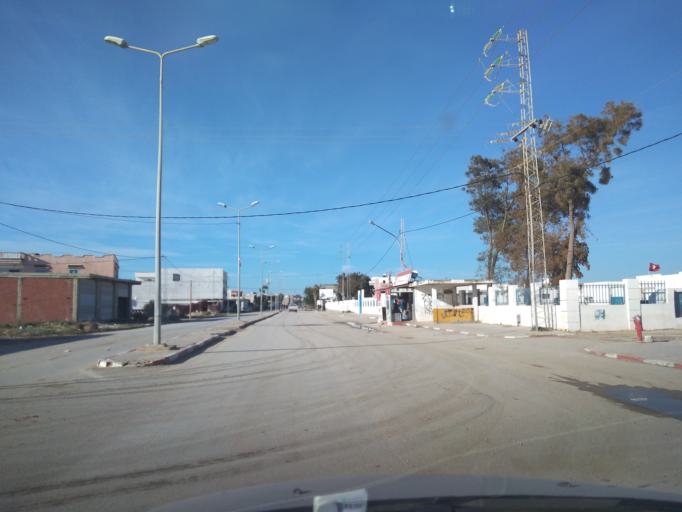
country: TN
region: Ariana
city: Qal'at al Andalus
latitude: 37.0530
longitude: 10.1221
